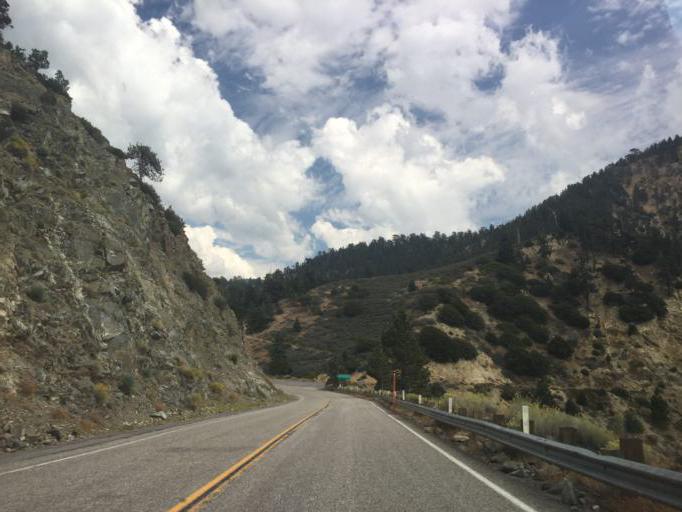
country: US
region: California
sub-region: Los Angeles County
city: Littlerock
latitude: 34.3568
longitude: -117.8532
